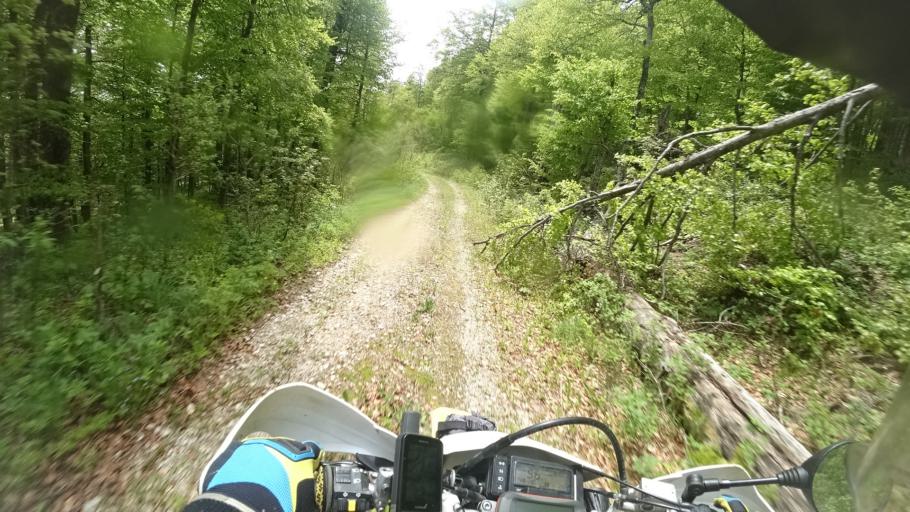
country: BA
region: Federation of Bosnia and Herzegovina
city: Orasac
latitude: 44.5699
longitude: 15.8771
